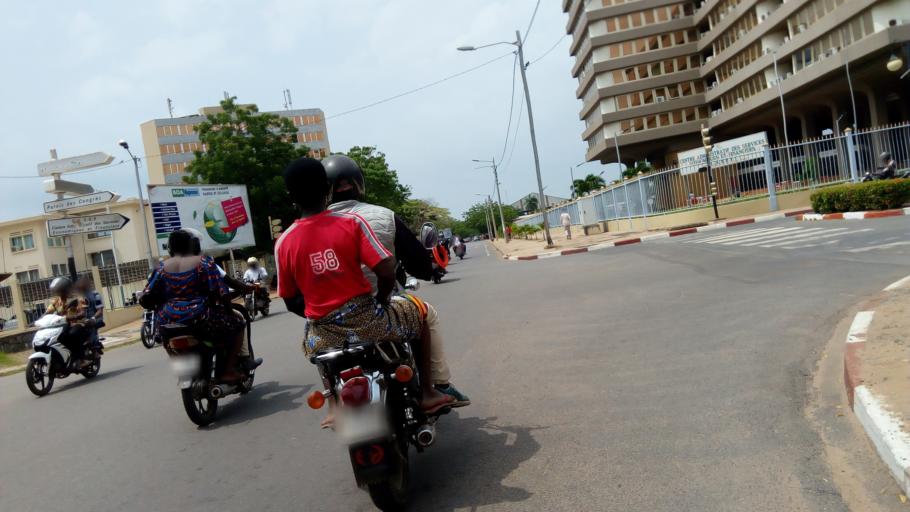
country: TG
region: Maritime
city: Lome
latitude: 6.1285
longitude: 1.2183
